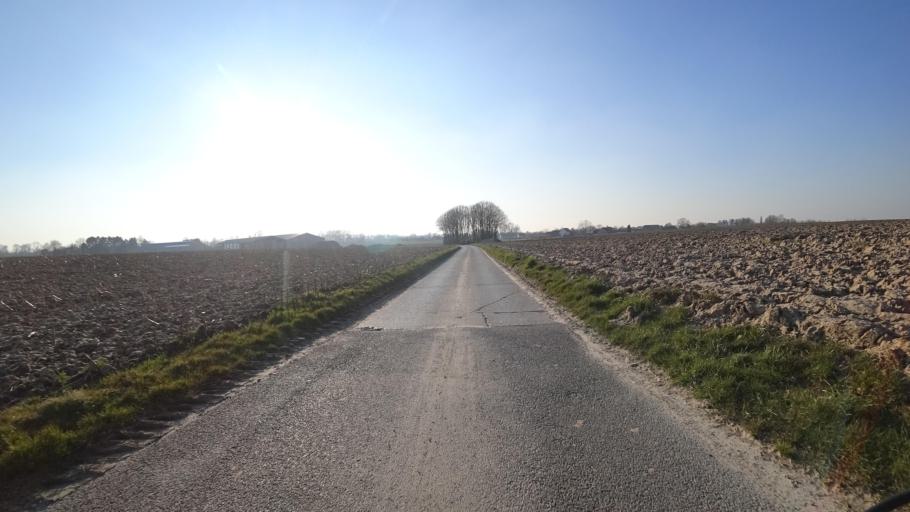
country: BE
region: Wallonia
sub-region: Province du Brabant Wallon
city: Chaumont-Gistoux
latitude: 50.6493
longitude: 4.7316
